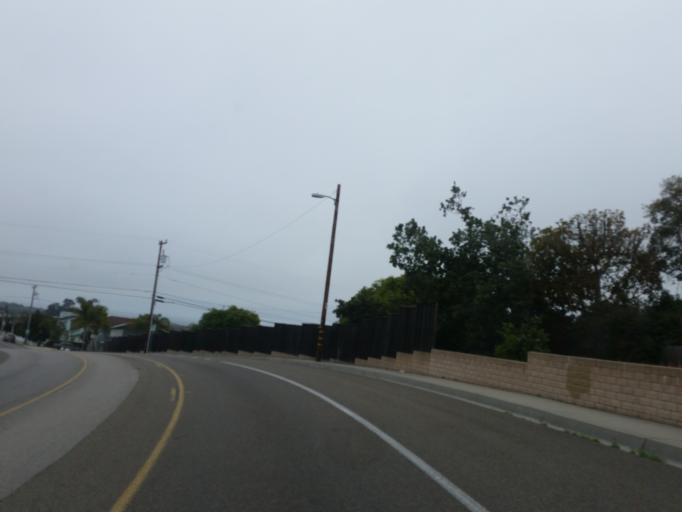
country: US
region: California
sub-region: San Luis Obispo County
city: Grover Beach
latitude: 35.1302
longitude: -120.6257
